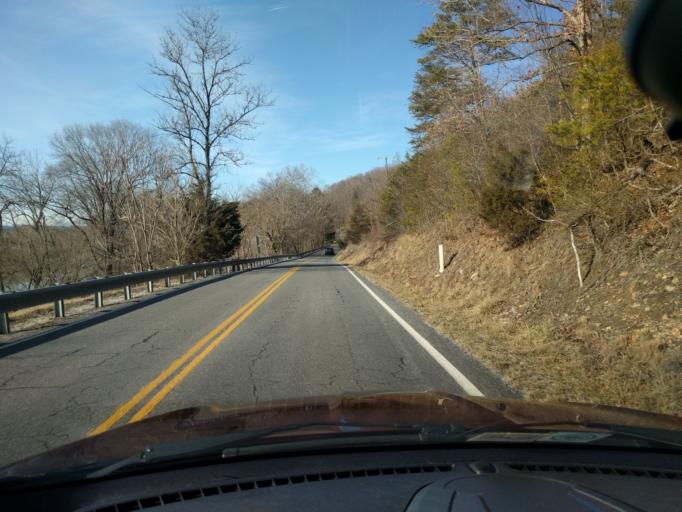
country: US
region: Virginia
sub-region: Botetourt County
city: Buchanan
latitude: 37.5276
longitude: -79.7070
